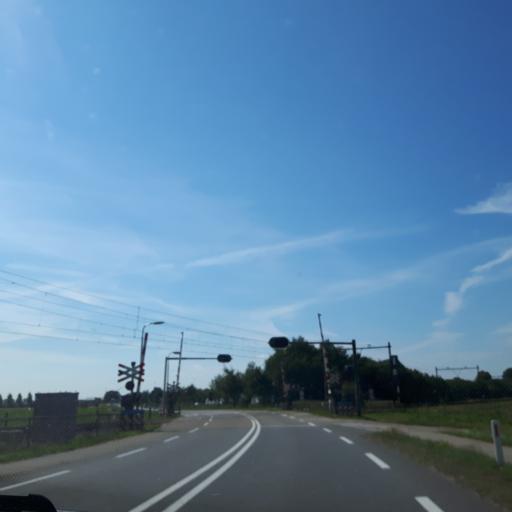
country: NL
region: Zeeland
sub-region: Gemeente Reimerswaal
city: Yerseke
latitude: 51.4276
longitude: 4.1323
